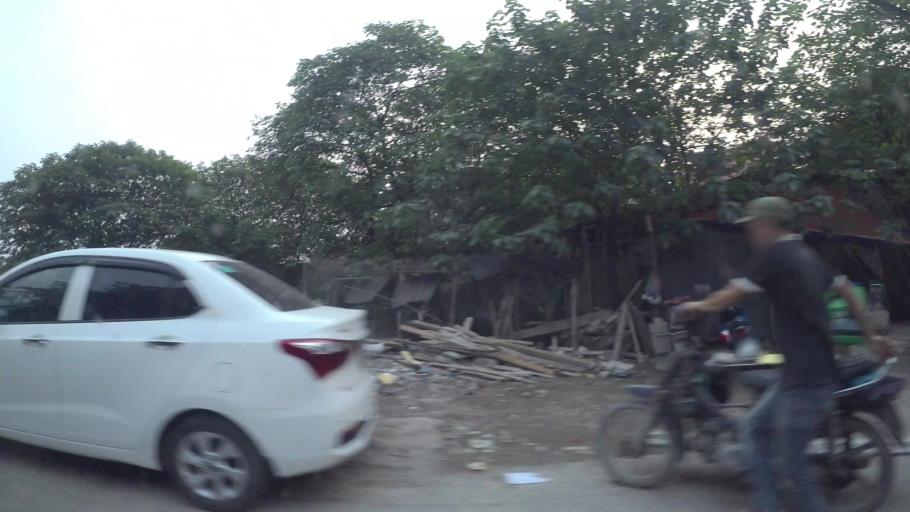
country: VN
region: Ha Noi
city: Thanh Xuan
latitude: 20.9793
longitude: 105.8069
